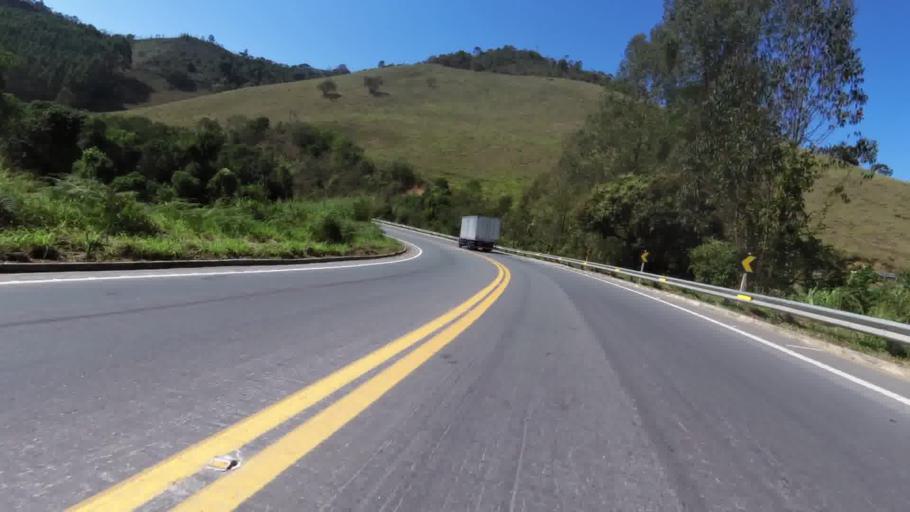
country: BR
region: Espirito Santo
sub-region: Marechal Floriano
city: Marechal Floriano
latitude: -20.4205
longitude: -40.8765
